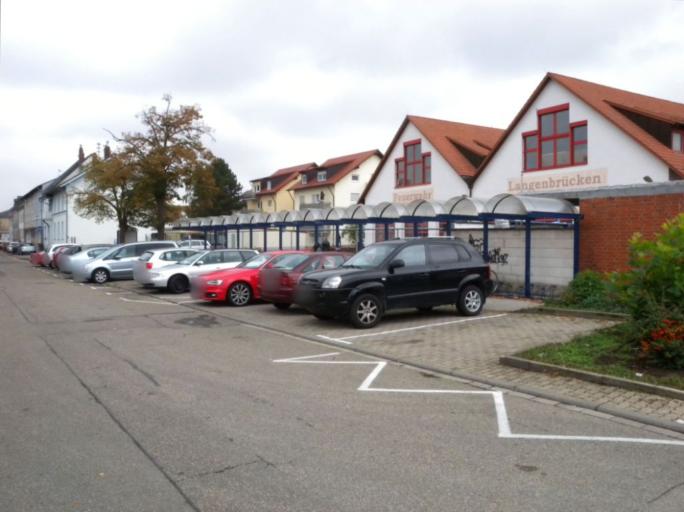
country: DE
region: Baden-Wuerttemberg
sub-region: Karlsruhe Region
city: Kronau
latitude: 49.1997
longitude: 8.6422
